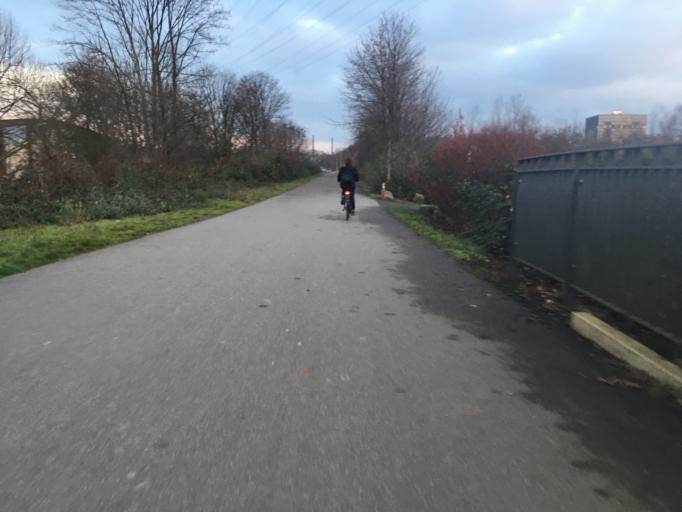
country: DE
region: North Rhine-Westphalia
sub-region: Regierungsbezirk Dusseldorf
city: Essen
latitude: 51.4659
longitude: 6.9833
